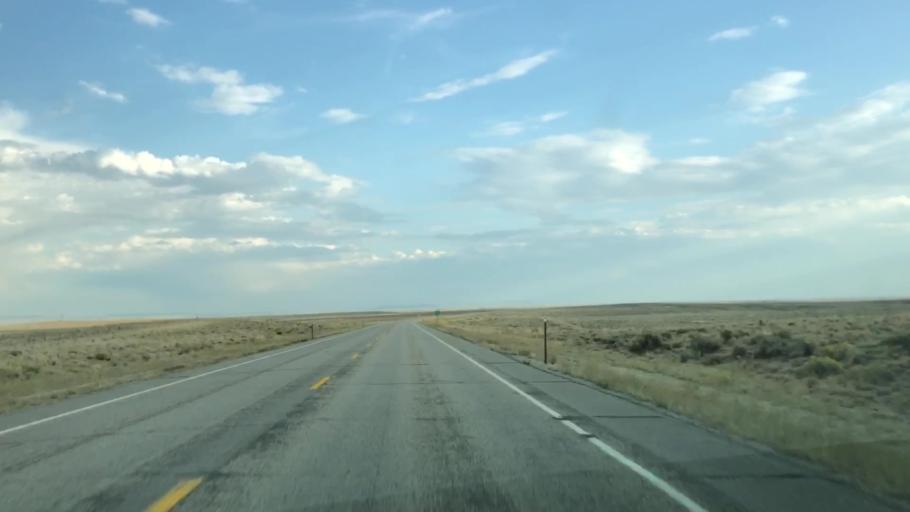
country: US
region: Wyoming
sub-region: Sweetwater County
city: North Rock Springs
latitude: 42.2596
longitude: -109.4713
